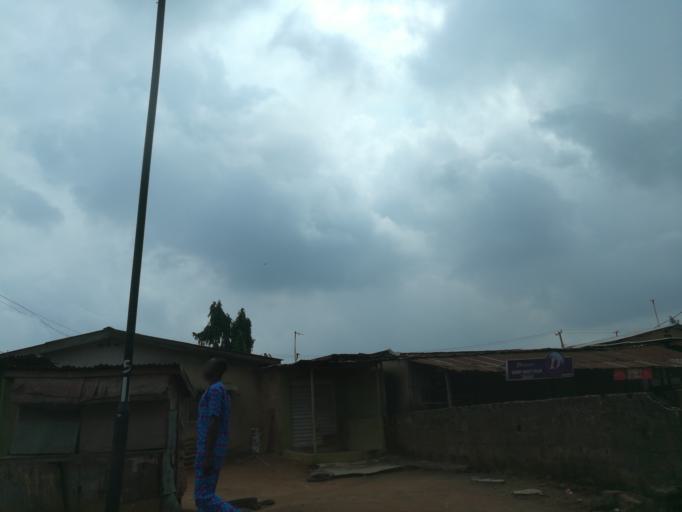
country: NG
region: Lagos
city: Oshodi
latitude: 6.5821
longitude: 3.3070
